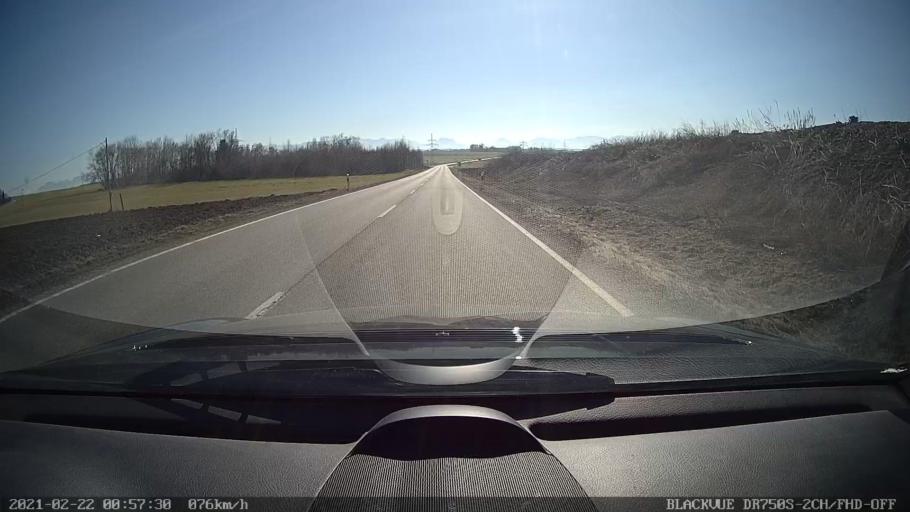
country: DE
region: Bavaria
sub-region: Upper Bavaria
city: Griesstatt
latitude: 47.9810
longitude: 12.1771
